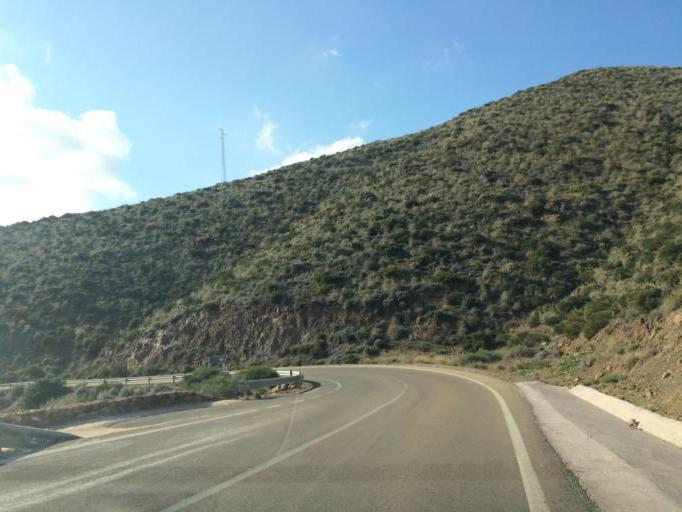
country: ES
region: Andalusia
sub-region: Provincia de Almeria
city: San Jose
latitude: 36.8279
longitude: -2.0398
